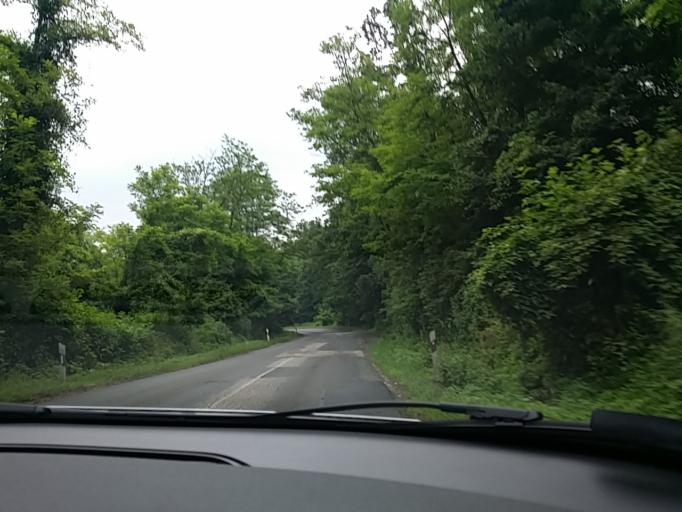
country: HU
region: Nograd
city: Matranovak
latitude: 48.0135
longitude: 20.0288
